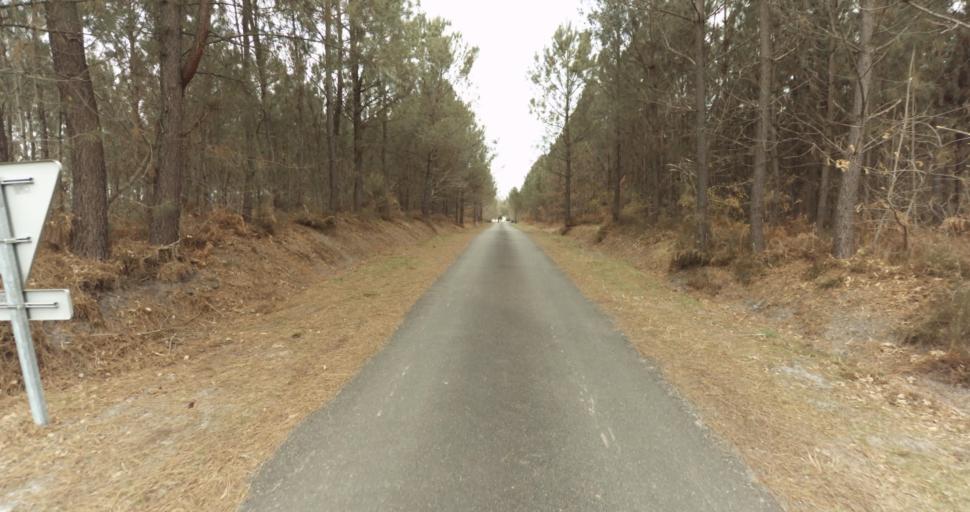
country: FR
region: Aquitaine
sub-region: Departement des Landes
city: Roquefort
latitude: 44.0593
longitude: -0.3913
